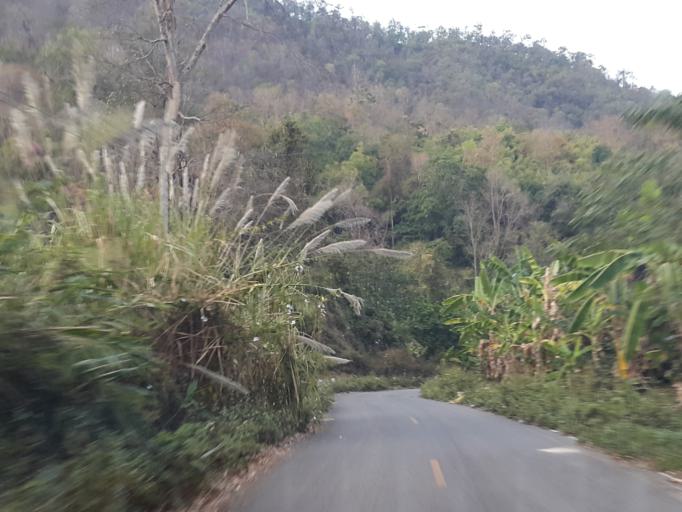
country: TH
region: Lampang
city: Mueang Pan
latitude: 18.8274
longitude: 99.4580
